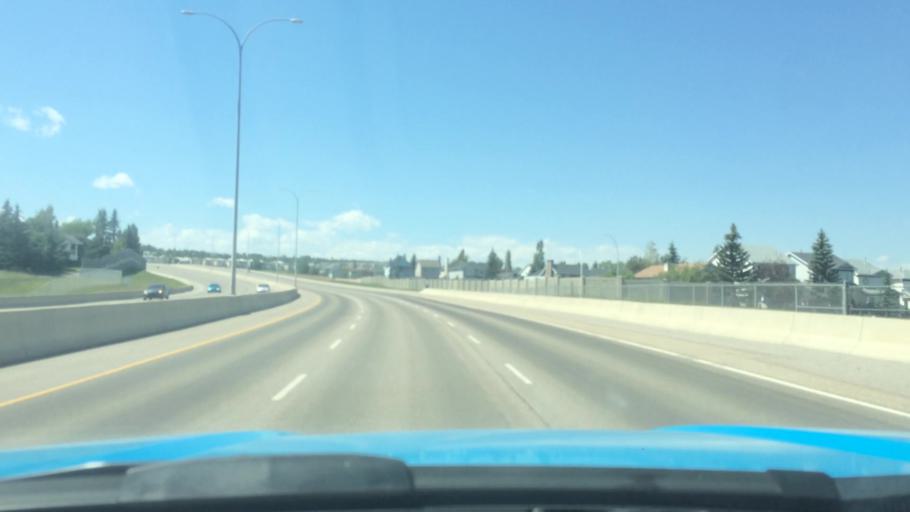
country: CA
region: Alberta
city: Calgary
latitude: 51.1444
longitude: -114.1141
